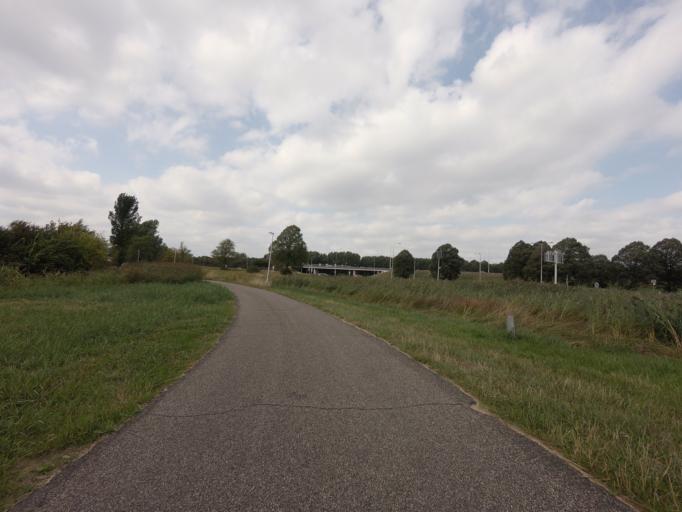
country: NL
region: Utrecht
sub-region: Gemeente Utrecht
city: Lunetten
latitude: 52.0550
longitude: 5.1207
